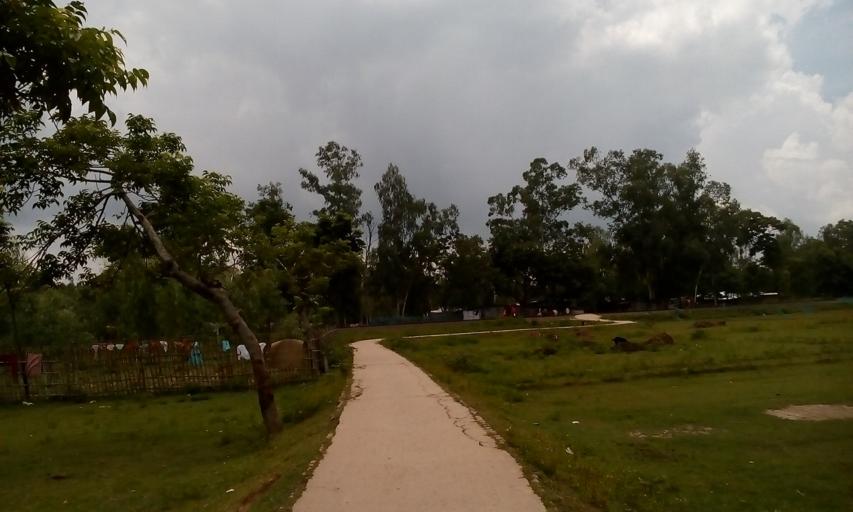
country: IN
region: West Bengal
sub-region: Dakshin Dinajpur
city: Balurghat
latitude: 25.3862
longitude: 88.9963
